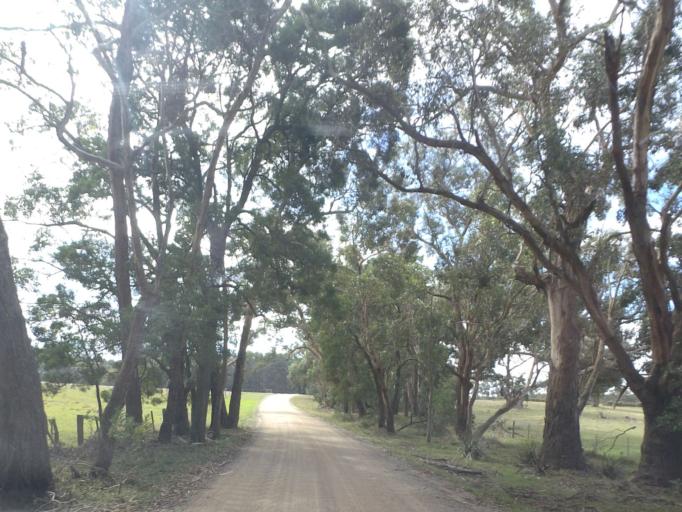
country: AU
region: Victoria
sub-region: Hume
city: Sunbury
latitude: -37.3711
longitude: 144.5515
